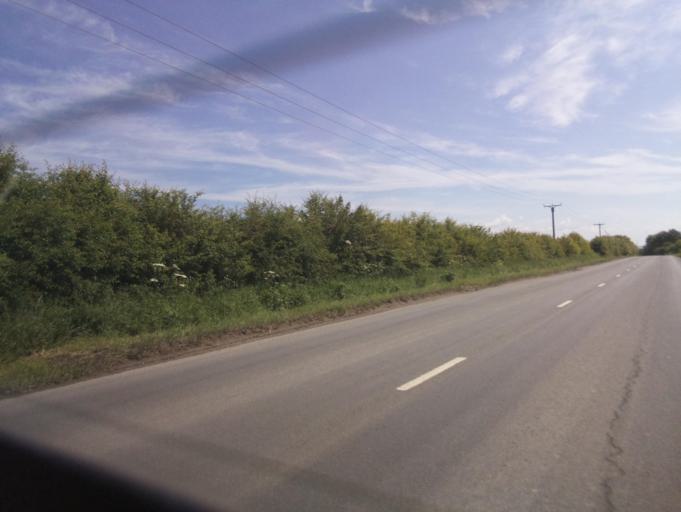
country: GB
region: England
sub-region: North Lincolnshire
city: Redbourne
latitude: 53.5014
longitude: -0.5599
